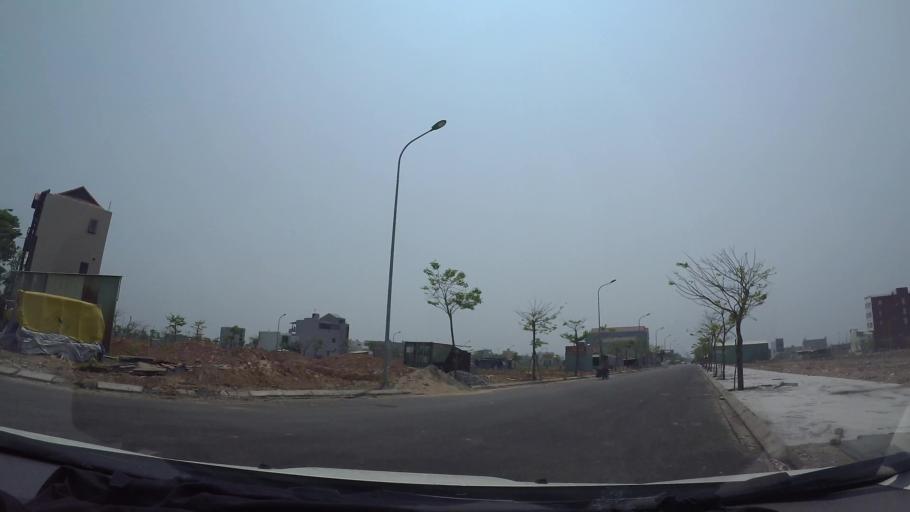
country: VN
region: Da Nang
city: Ngu Hanh Son
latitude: 16.0130
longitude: 108.2416
